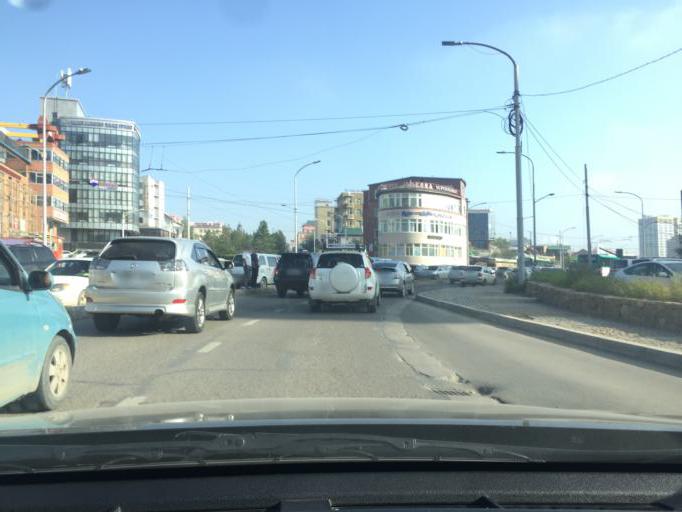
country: MN
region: Ulaanbaatar
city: Ulaanbaatar
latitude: 47.9156
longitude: 106.8948
